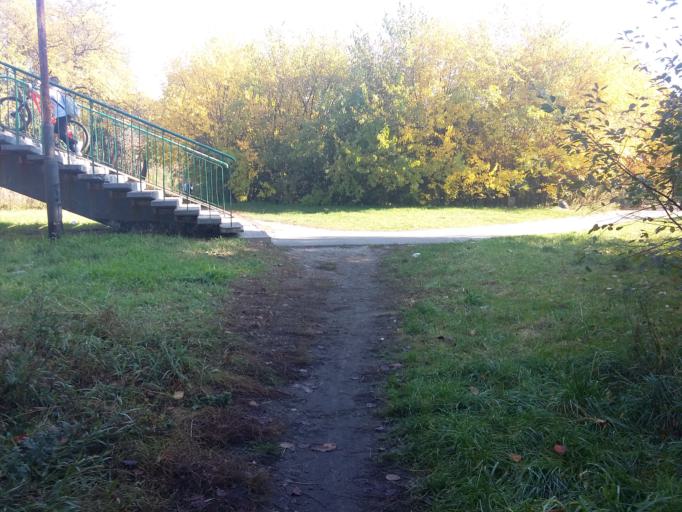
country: PL
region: Lodz Voivodeship
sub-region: Powiat pabianicki
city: Ksawerow
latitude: 51.7404
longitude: 19.4072
